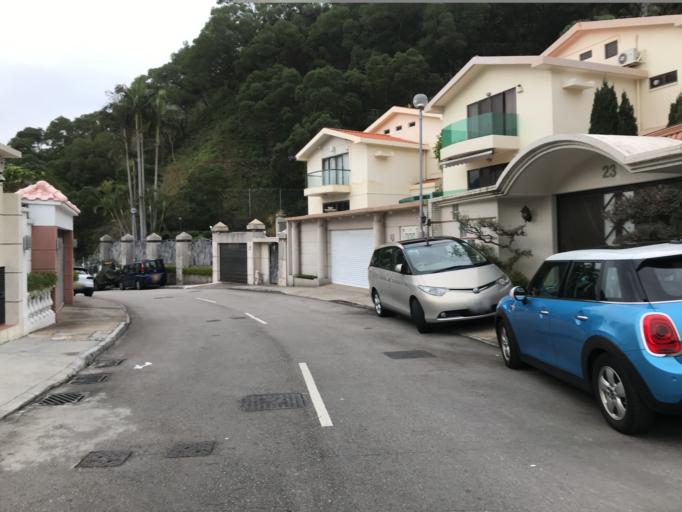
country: HK
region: Tai Po
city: Tai Po
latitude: 22.4642
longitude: 114.1602
